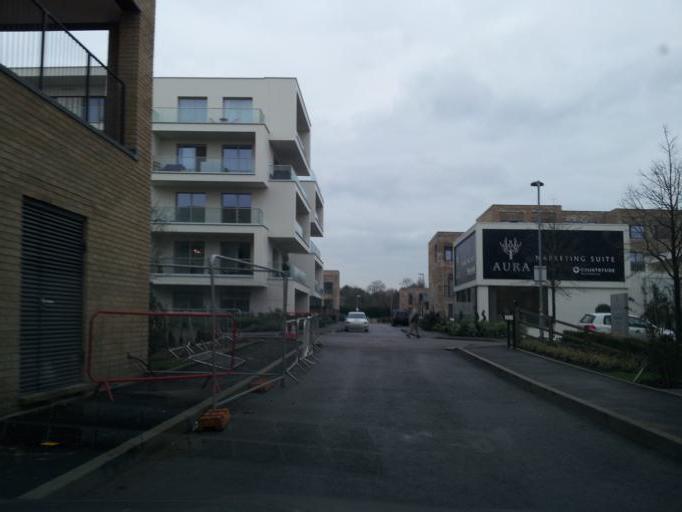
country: GB
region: England
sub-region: Cambridgeshire
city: Cambridge
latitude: 52.1791
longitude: 0.1236
